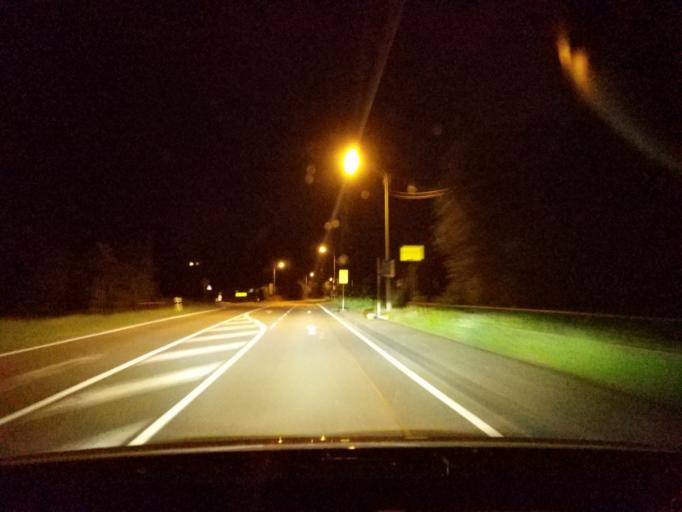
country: DE
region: Rheinland-Pfalz
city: Katzweiler
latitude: 49.5055
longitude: 7.6904
